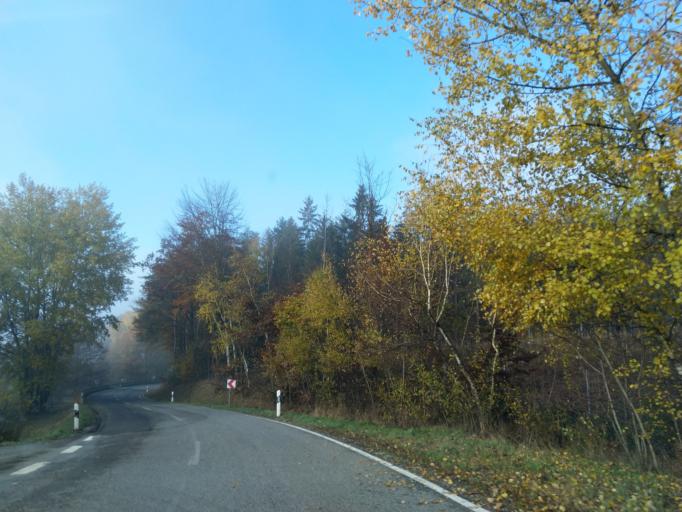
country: DE
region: Bavaria
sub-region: Lower Bavaria
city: Aussernzell
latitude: 48.7278
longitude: 13.1906
